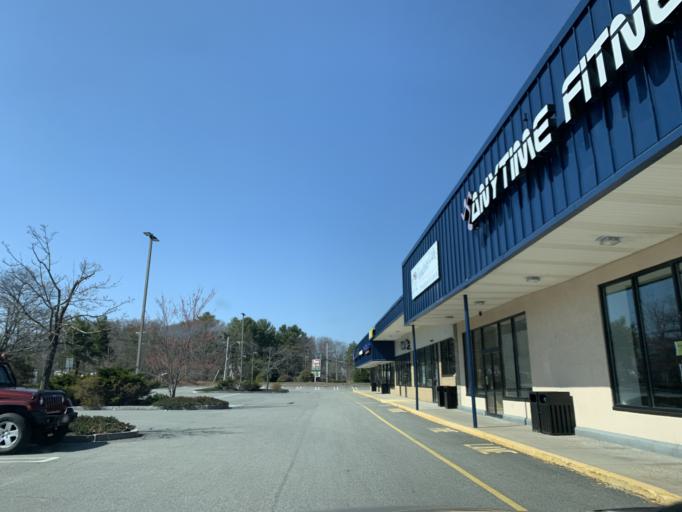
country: US
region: Massachusetts
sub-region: Norfolk County
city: Plainville
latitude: 42.0118
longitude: -71.3054
